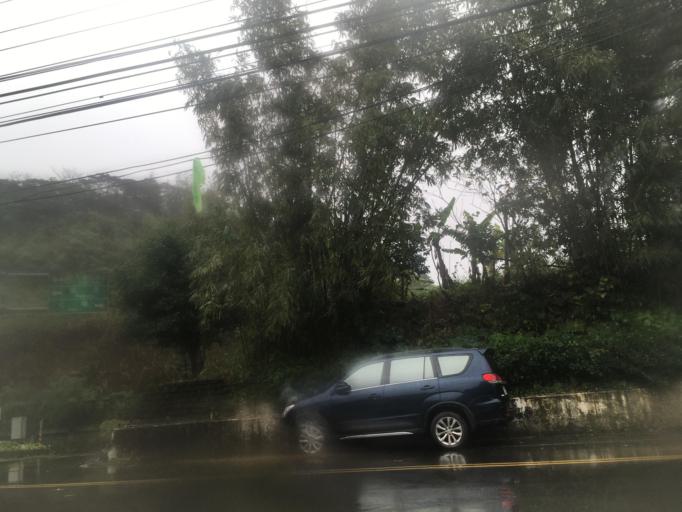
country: TW
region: Taiwan
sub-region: Keelung
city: Keelung
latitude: 25.1116
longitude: 121.6891
